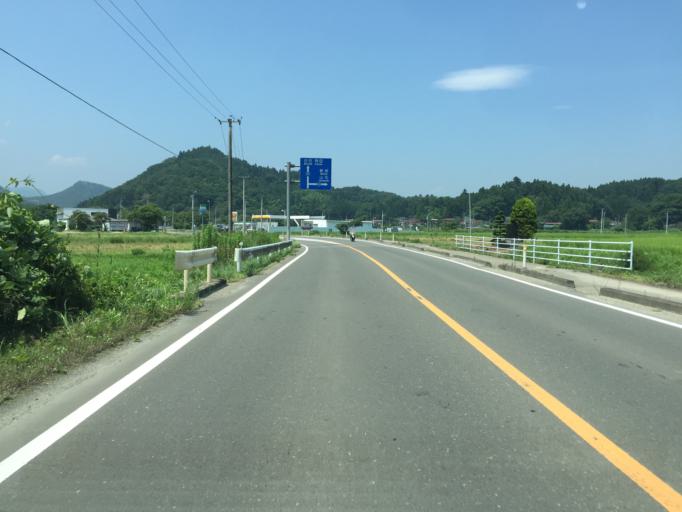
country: JP
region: Miyagi
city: Marumori
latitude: 37.8887
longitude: 140.8140
